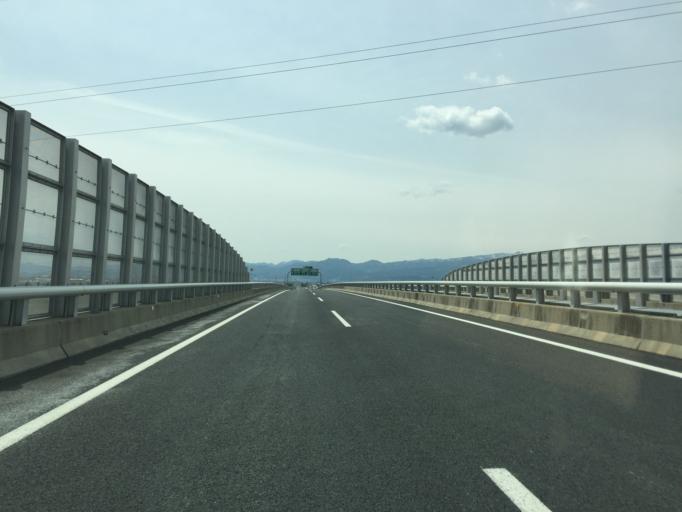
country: JP
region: Yamagata
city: Tendo
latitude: 38.3111
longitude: 140.3182
